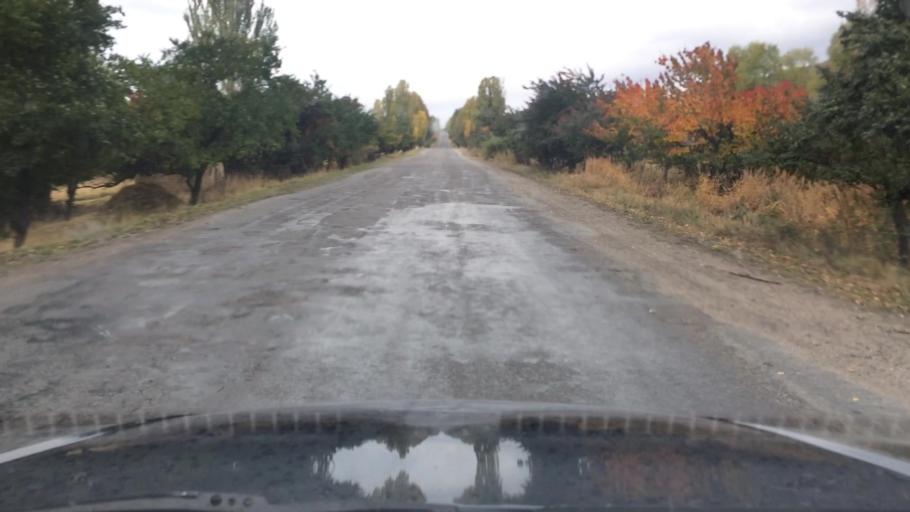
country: KG
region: Ysyk-Koel
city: Pokrovka
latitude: 42.7360
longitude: 77.9647
